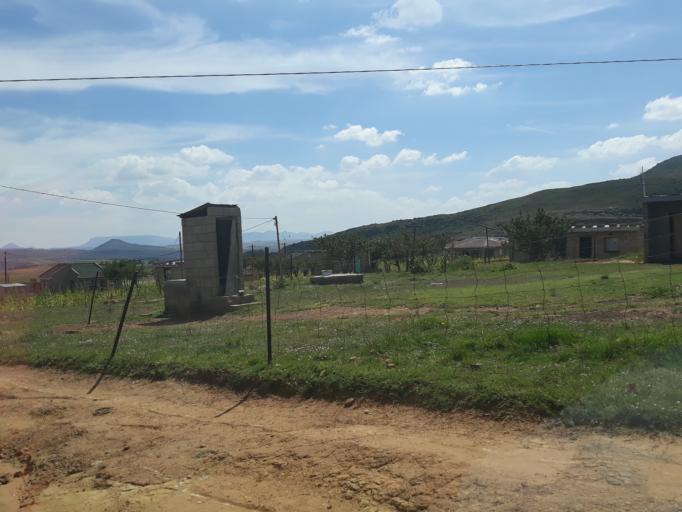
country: LS
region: Mohale's Hoek District
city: Mohale's Hoek
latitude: -30.1025
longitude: 27.4672
